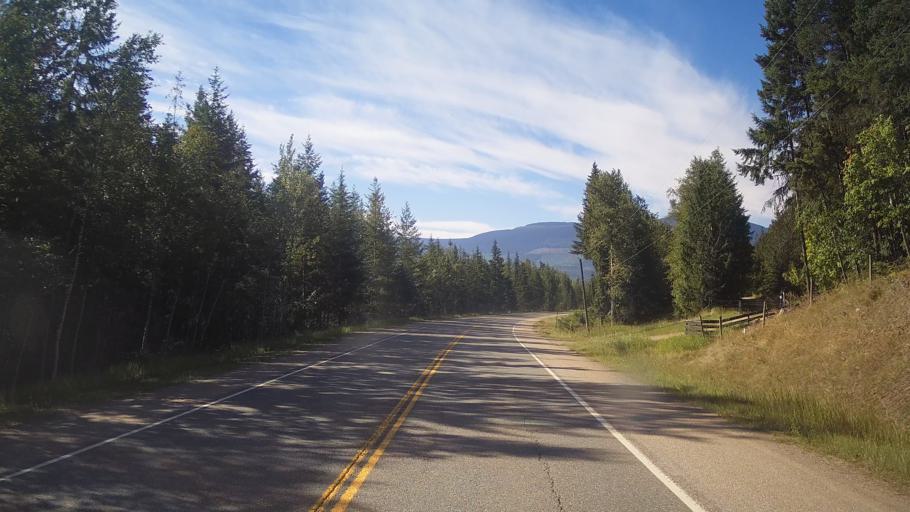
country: CA
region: British Columbia
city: Chase
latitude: 51.6314
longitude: -119.6958
